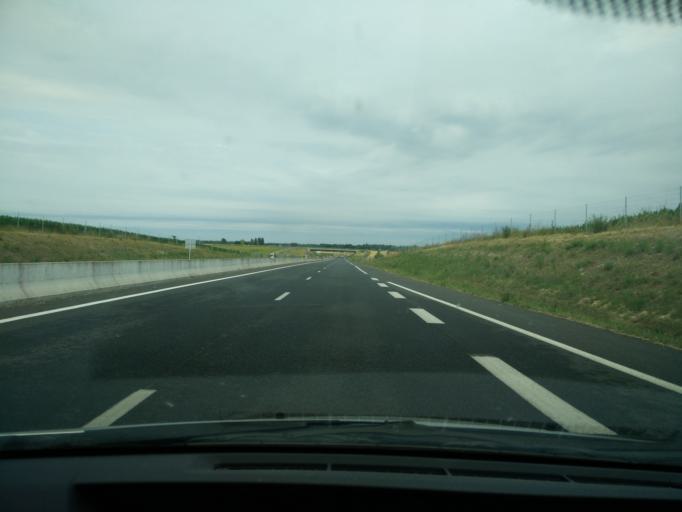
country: FR
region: Pays de la Loire
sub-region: Departement de Maine-et-Loire
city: Saint-Jean
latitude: 47.2882
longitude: -0.3783
